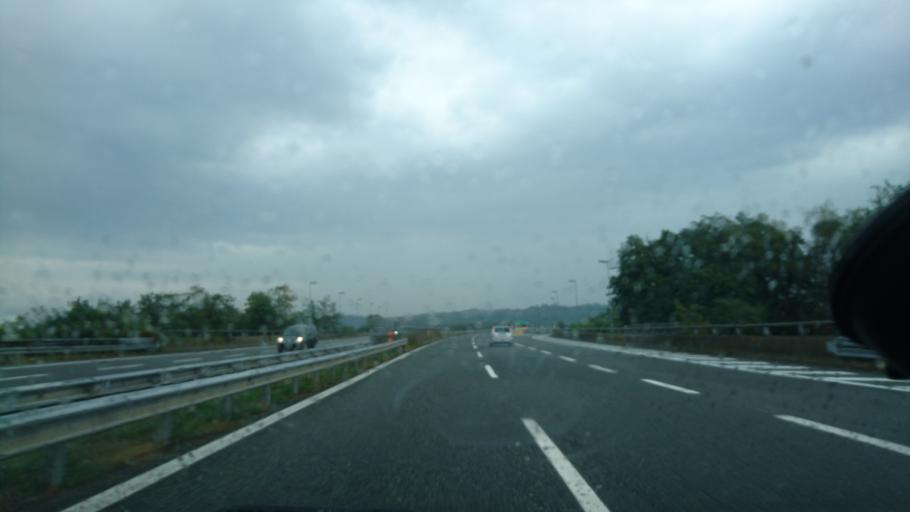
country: IT
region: Piedmont
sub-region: Provincia di Novara
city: Ghemme
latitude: 45.6050
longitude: 8.4046
